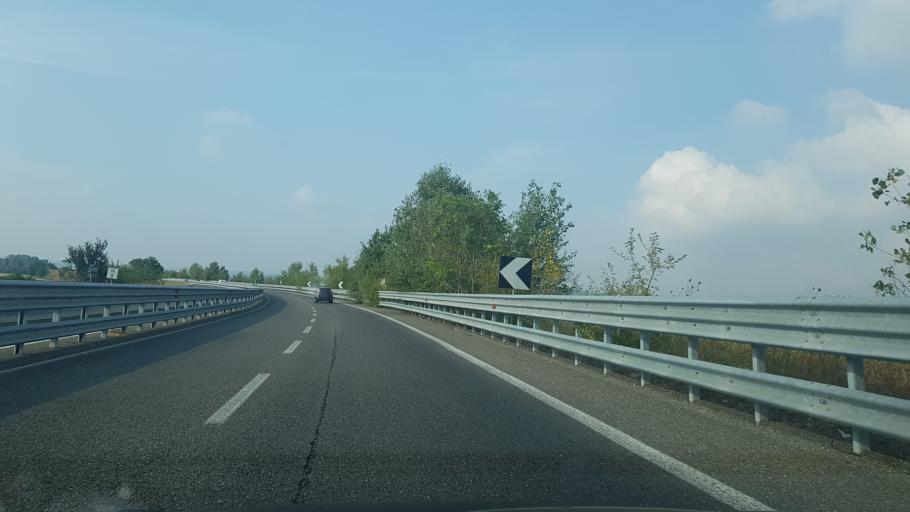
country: IT
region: Piedmont
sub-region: Provincia di Alessandria
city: Alessandria
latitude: 44.9109
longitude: 8.6423
